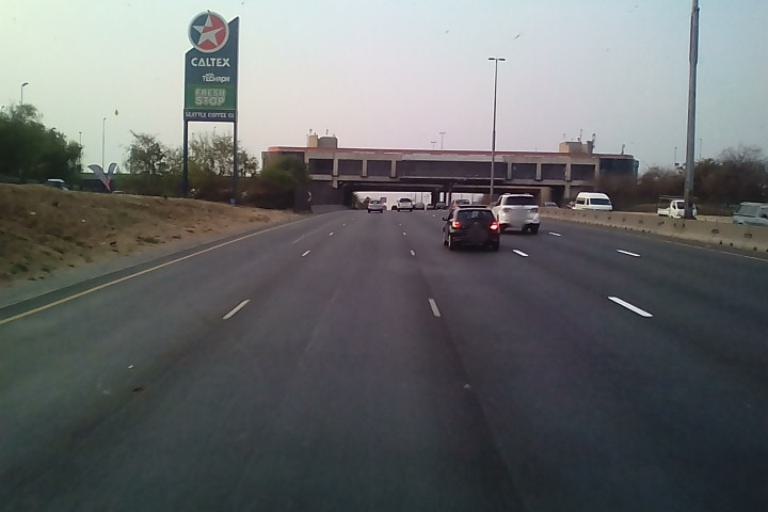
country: ZA
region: Gauteng
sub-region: City of Johannesburg Metropolitan Municipality
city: Midrand
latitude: -25.9826
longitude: 28.1254
